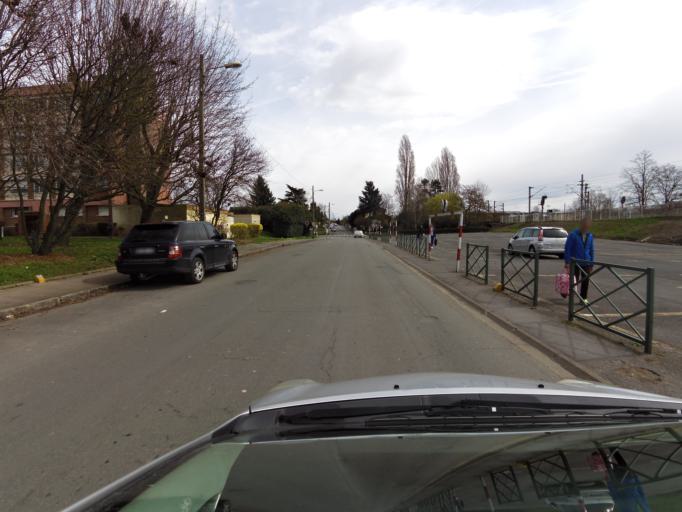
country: FR
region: Ile-de-France
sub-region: Departement de Seine-et-Marne
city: Villeparisis
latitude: 48.9539
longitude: 2.6041
